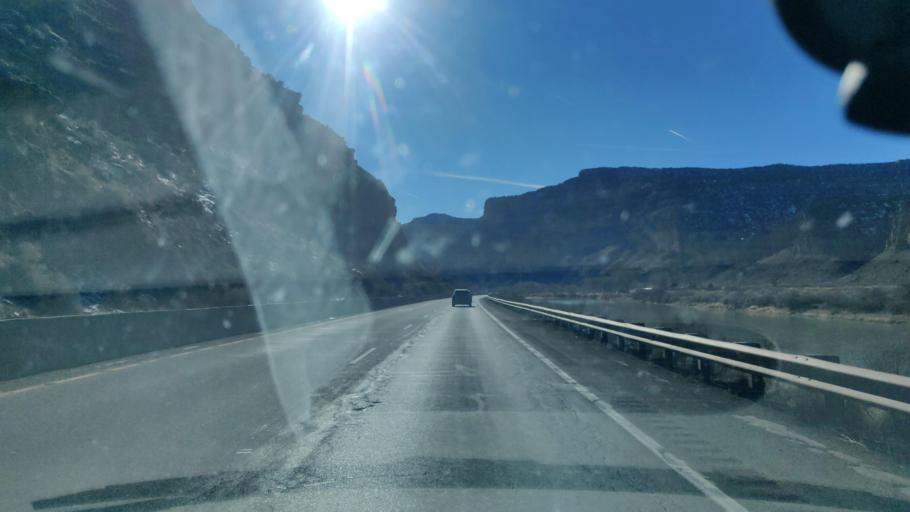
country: US
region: Colorado
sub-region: Mesa County
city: Palisade
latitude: 39.1771
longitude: -108.2879
